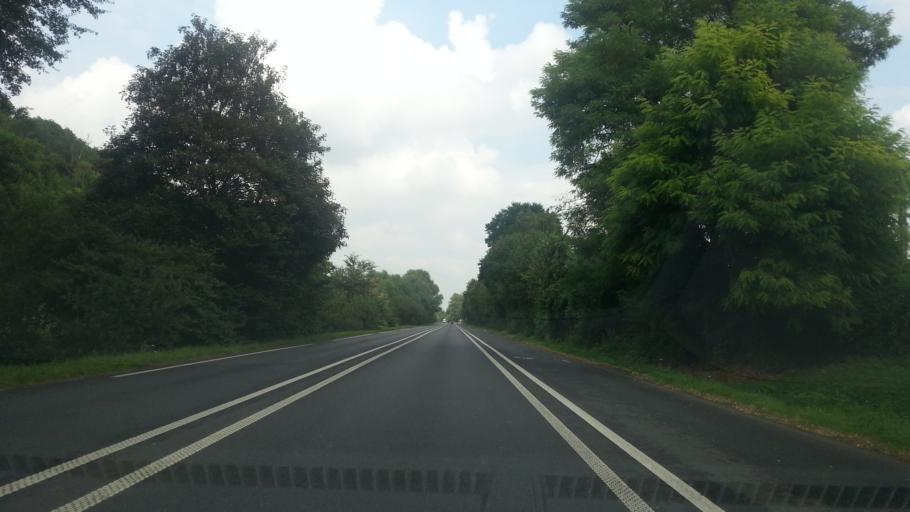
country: FR
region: Picardie
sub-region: Departement de l'Oise
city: Saint-Maximin
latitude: 49.2283
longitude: 2.4321
